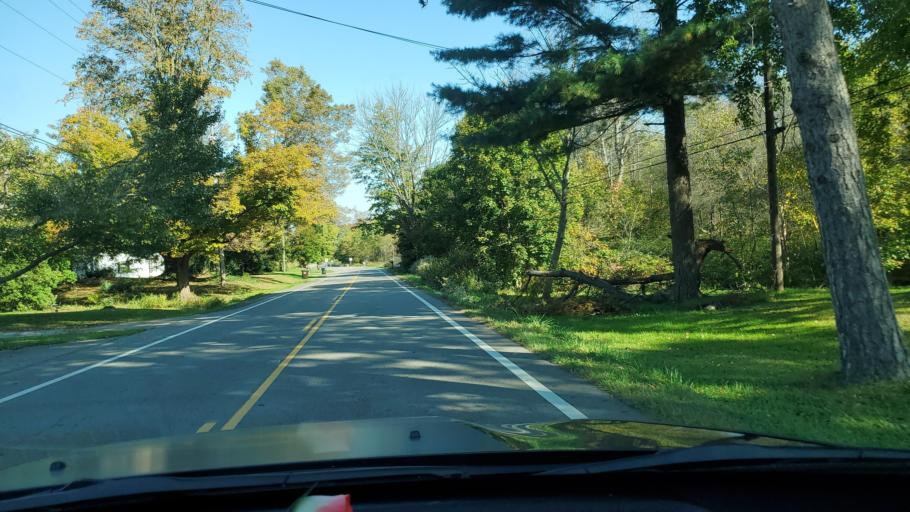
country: US
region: Ohio
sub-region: Trumbull County
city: Brookfield Center
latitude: 41.3910
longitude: -80.5684
